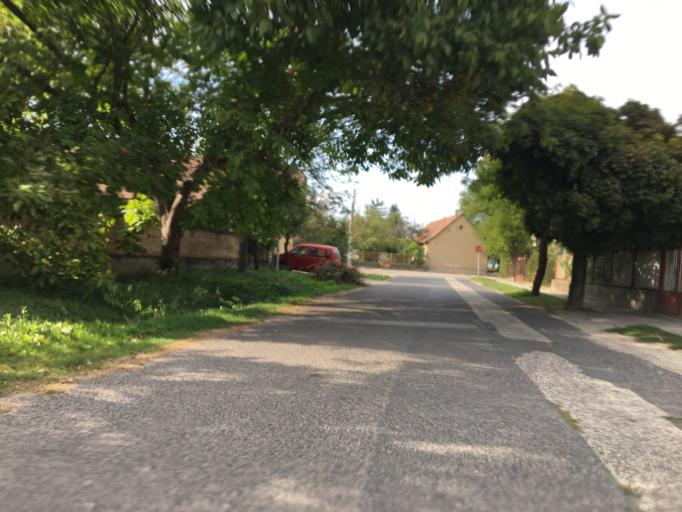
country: HU
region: Pest
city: Szigetszentmiklos
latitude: 47.3545
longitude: 19.0420
